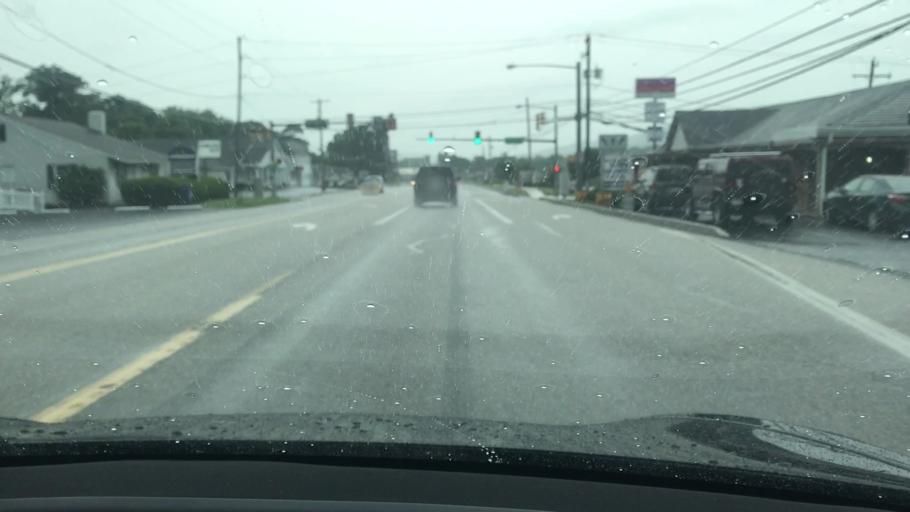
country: US
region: Pennsylvania
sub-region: Dauphin County
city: Lawrence Park
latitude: 40.3366
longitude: -76.8194
